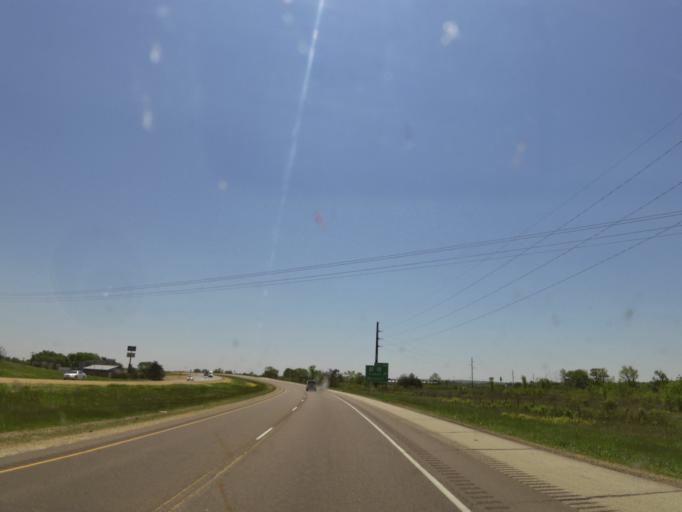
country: US
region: Wisconsin
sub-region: Monroe County
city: Tomah
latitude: 44.0255
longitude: -90.5112
